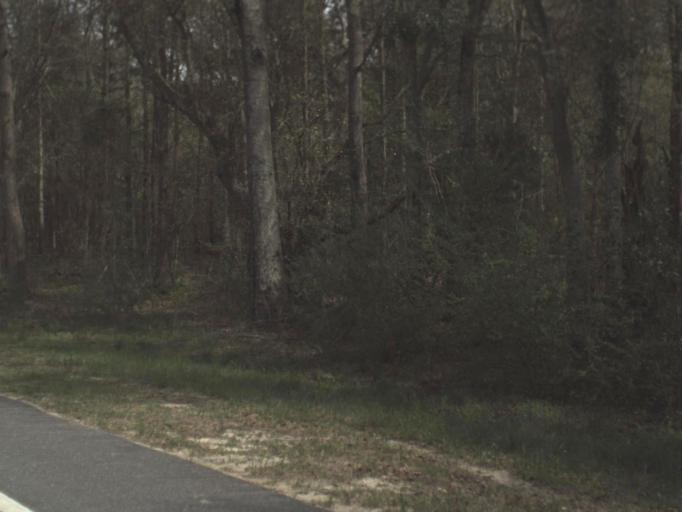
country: US
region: Florida
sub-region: Jackson County
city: Graceville
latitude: 30.9638
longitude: -85.6499
